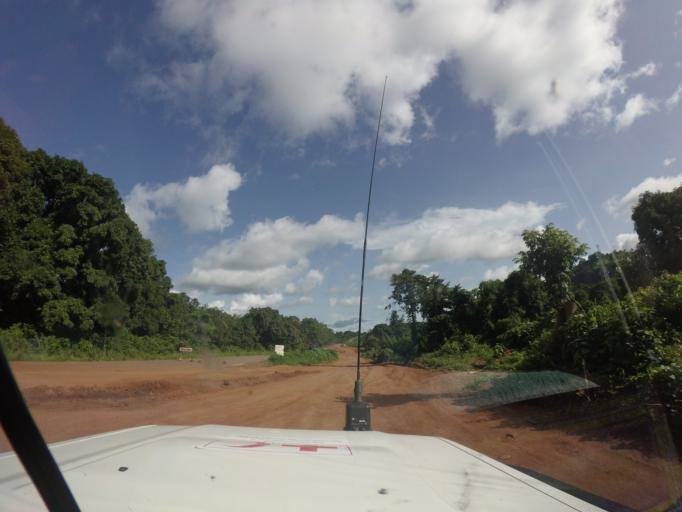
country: GN
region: Mamou
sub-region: Mamou Prefecture
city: Mamou
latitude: 10.2402
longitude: -12.4568
